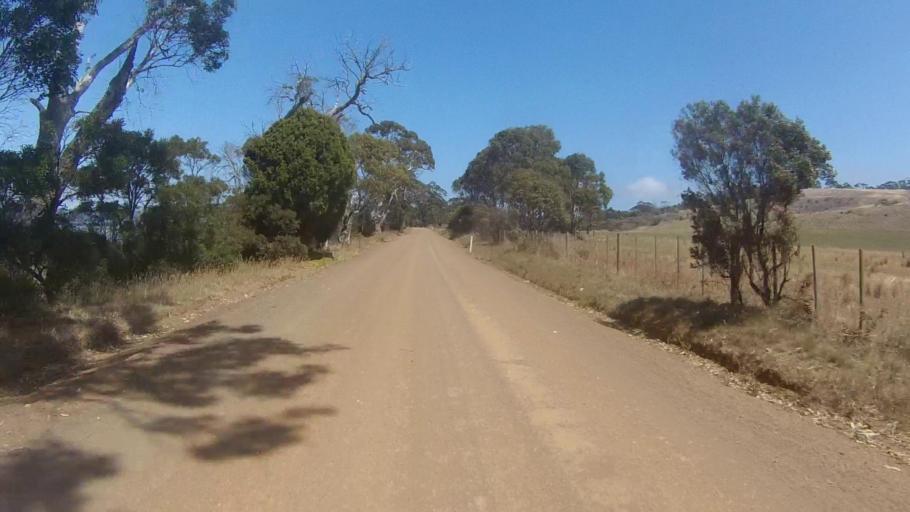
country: AU
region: Tasmania
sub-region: Sorell
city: Sorell
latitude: -42.8306
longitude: 147.8567
